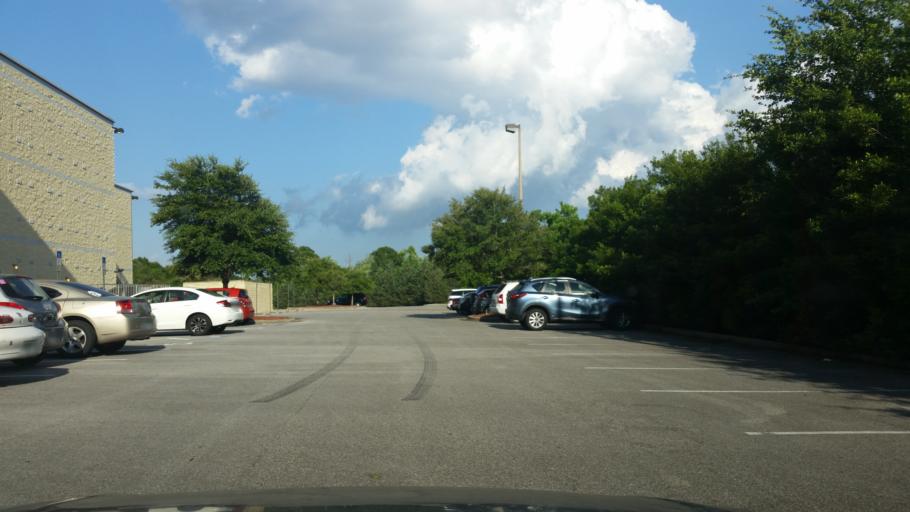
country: US
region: Florida
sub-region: Escambia County
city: Brent
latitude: 30.4722
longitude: -87.2173
